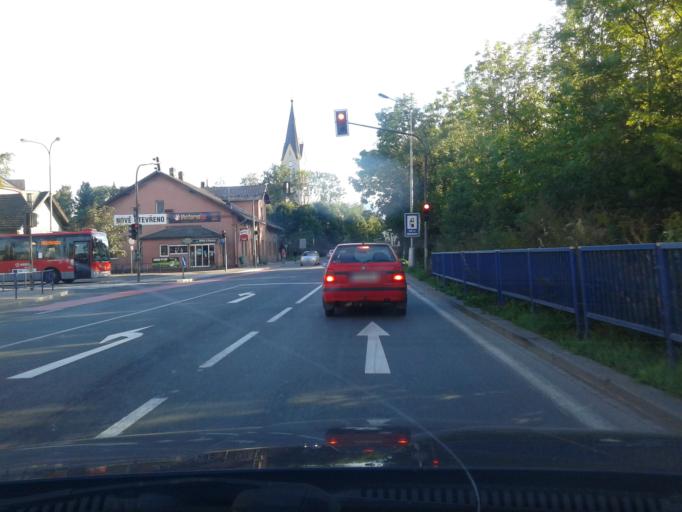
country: CZ
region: Moravskoslezsky
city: Trinec
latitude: 49.6803
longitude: 18.6660
